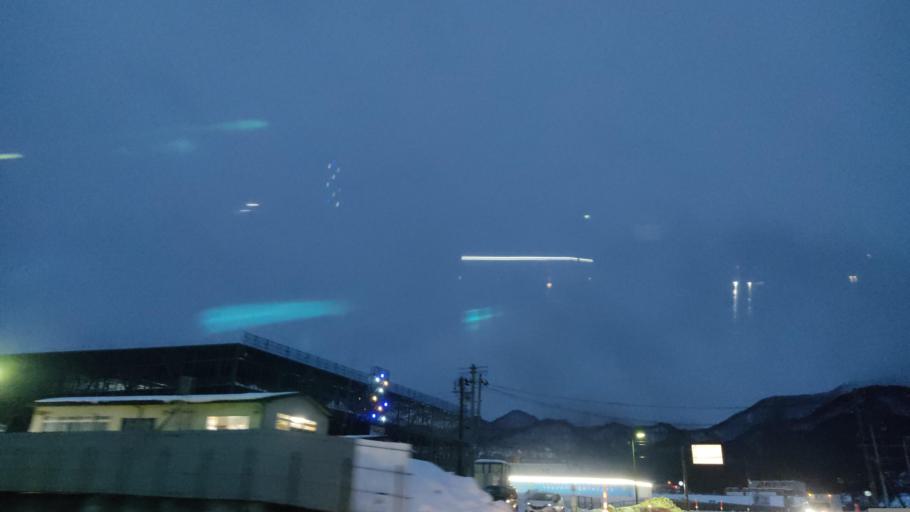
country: JP
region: Iwate
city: Morioka-shi
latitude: 39.6320
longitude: 141.1017
